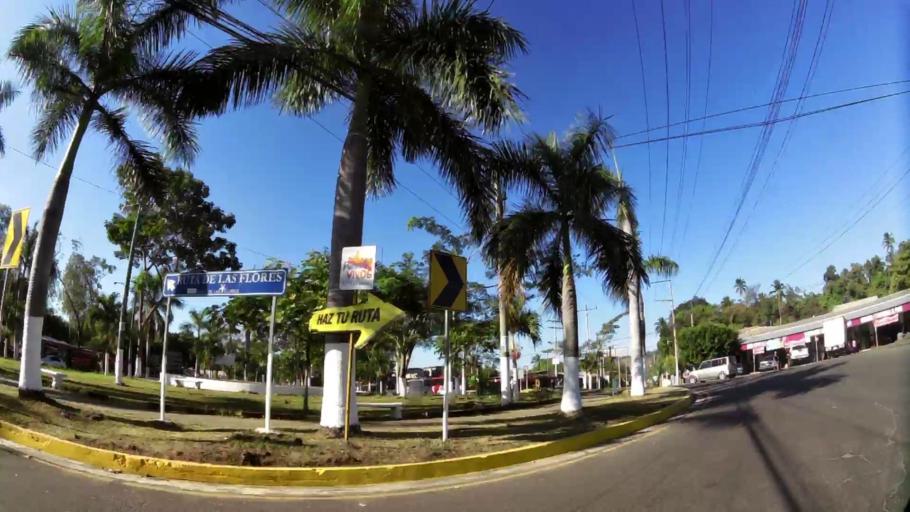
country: SV
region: Sonsonate
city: Sonzacate
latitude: 13.7380
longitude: -89.7096
